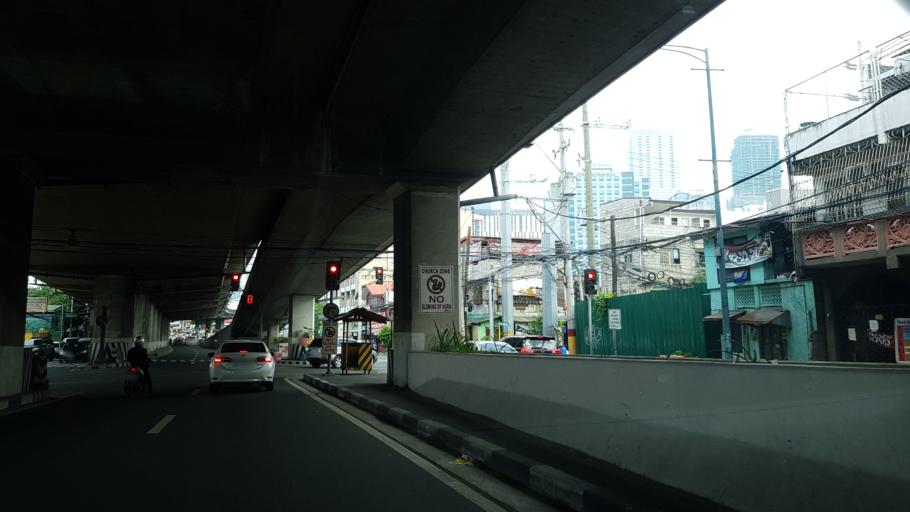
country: PH
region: Metro Manila
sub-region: Makati City
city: Makati City
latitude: 14.5574
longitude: 121.0398
